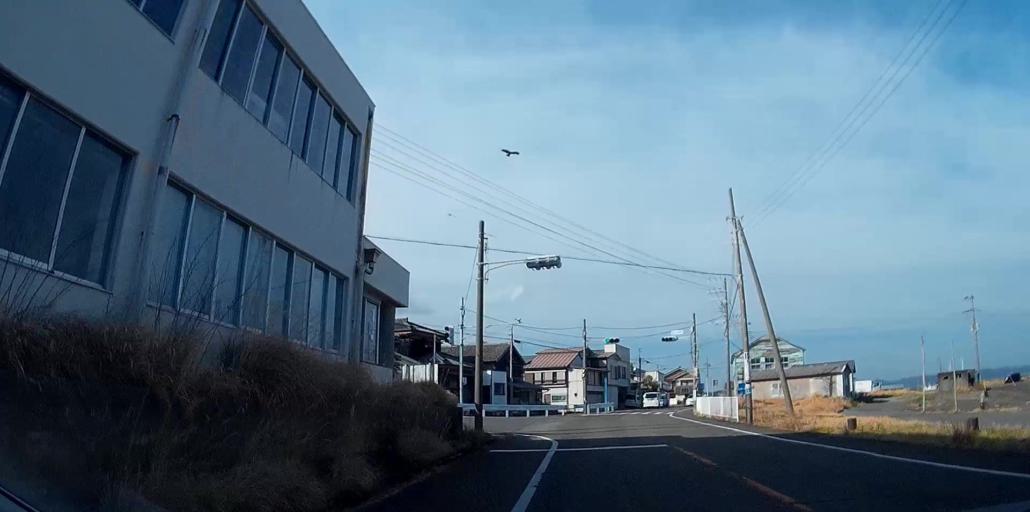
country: JP
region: Chiba
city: Tateyama
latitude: 34.9591
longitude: 139.9618
